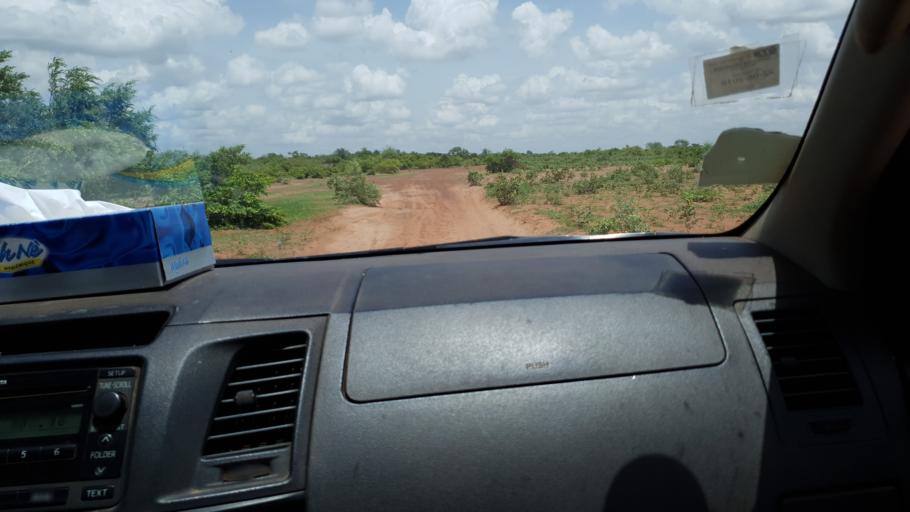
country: ML
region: Koulikoro
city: Banamba
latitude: 13.3785
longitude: -7.2072
